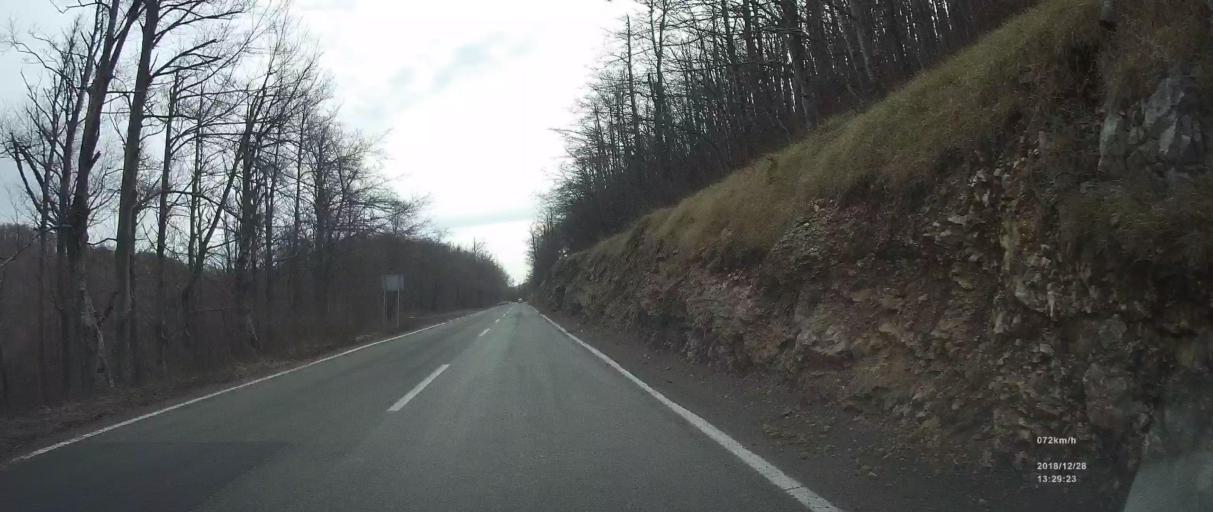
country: HR
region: Primorsko-Goranska
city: Hreljin
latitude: 45.3615
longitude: 14.6280
